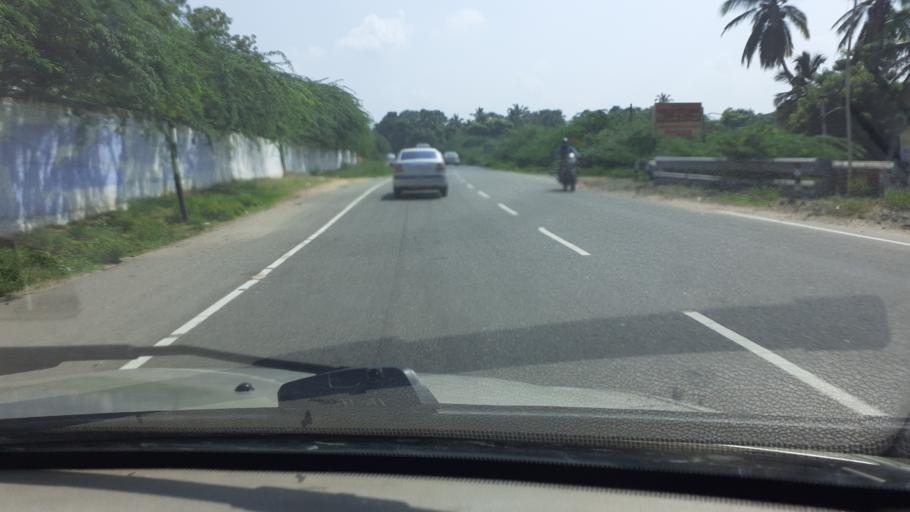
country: IN
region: Tamil Nadu
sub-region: Thoothukkudi
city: Alwar Tirunagari
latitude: 8.6086
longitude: 77.9326
